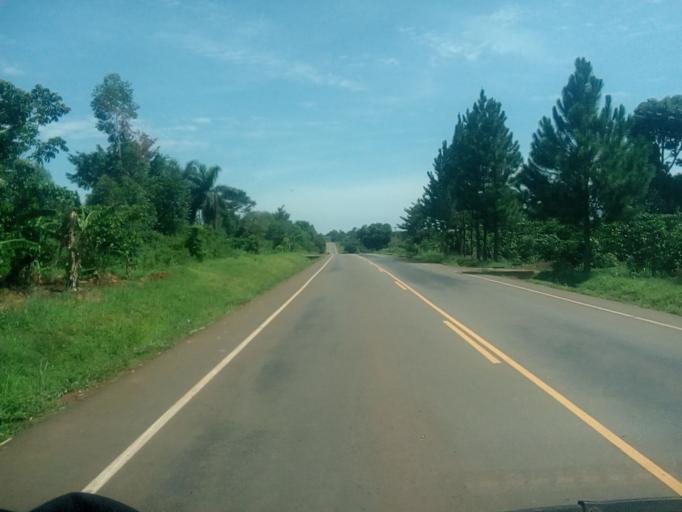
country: UG
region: Eastern Region
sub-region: Luuka District
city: Luuka Town
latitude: 0.8221
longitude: 33.2364
